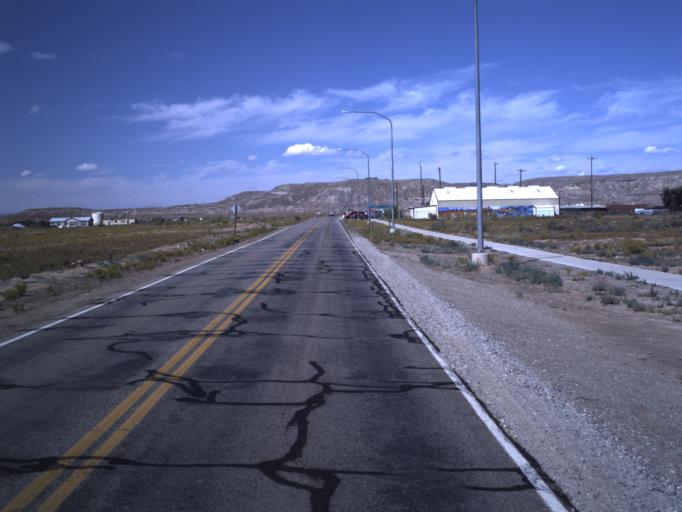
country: US
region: Utah
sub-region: San Juan County
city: Blanding
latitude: 37.2633
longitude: -109.3076
